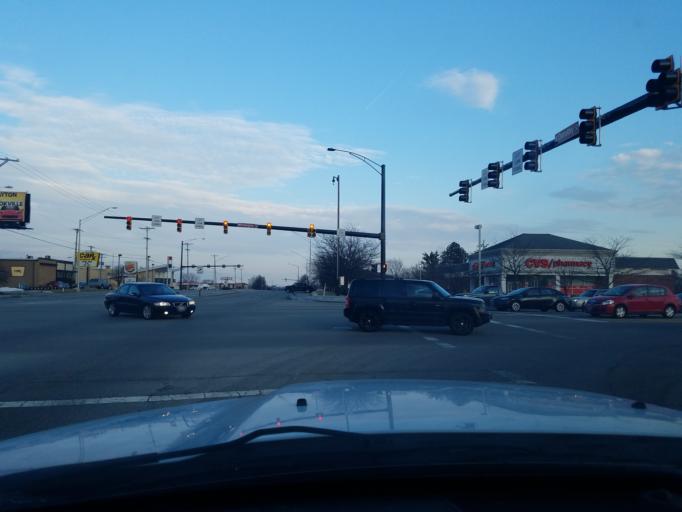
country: US
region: Ohio
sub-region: Montgomery County
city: Kettering
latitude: 39.7036
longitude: -84.1422
